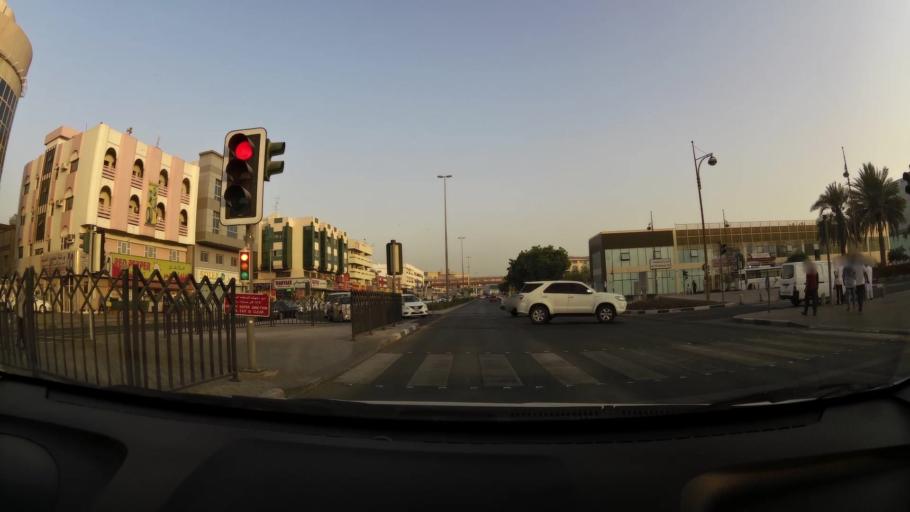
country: AE
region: Ash Shariqah
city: Sharjah
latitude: 25.2749
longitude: 55.3292
